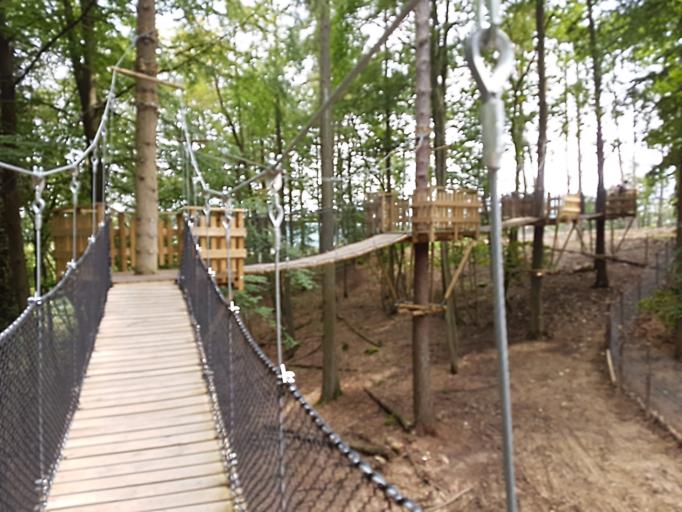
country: BE
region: Wallonia
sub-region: Province du Luxembourg
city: Tellin
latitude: 50.1197
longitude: 5.1971
